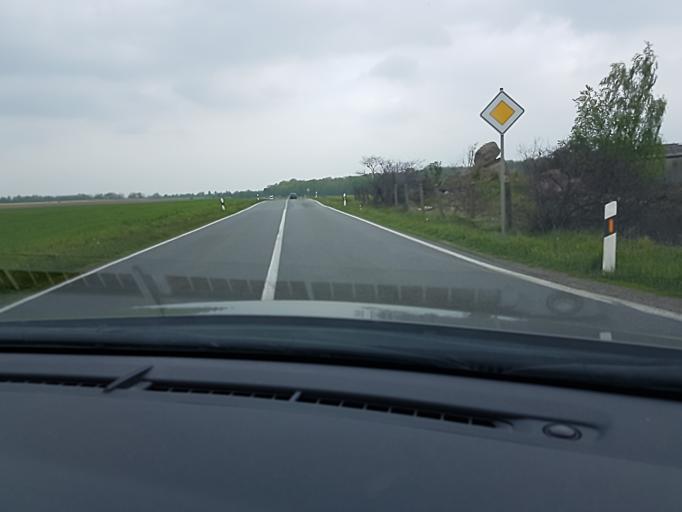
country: DE
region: Saxony
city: Belgern
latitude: 51.4620
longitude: 13.1546
